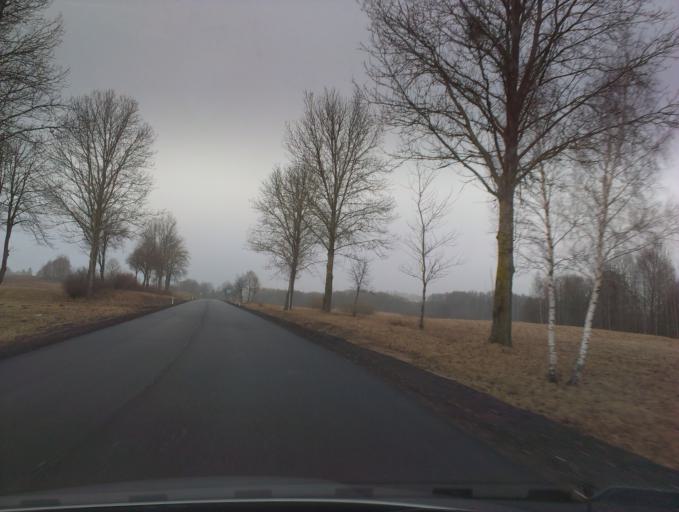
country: PL
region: West Pomeranian Voivodeship
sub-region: Powiat koszalinski
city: Bobolice
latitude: 53.9430
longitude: 16.5905
